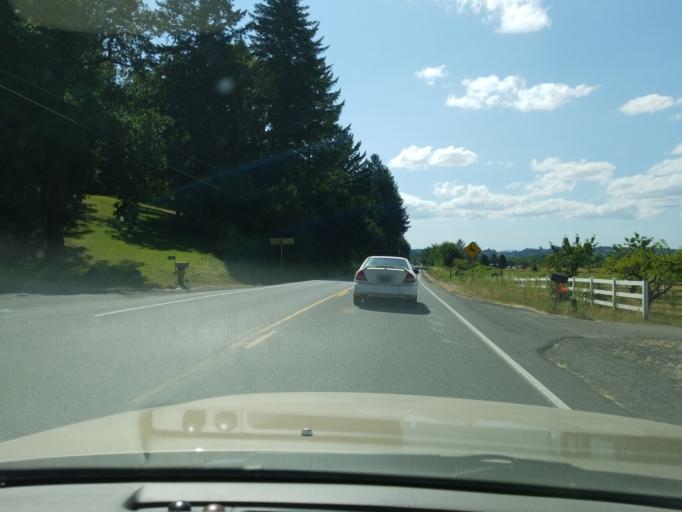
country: US
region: Oregon
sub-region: Yamhill County
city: Dundee
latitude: 45.3167
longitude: -123.0417
